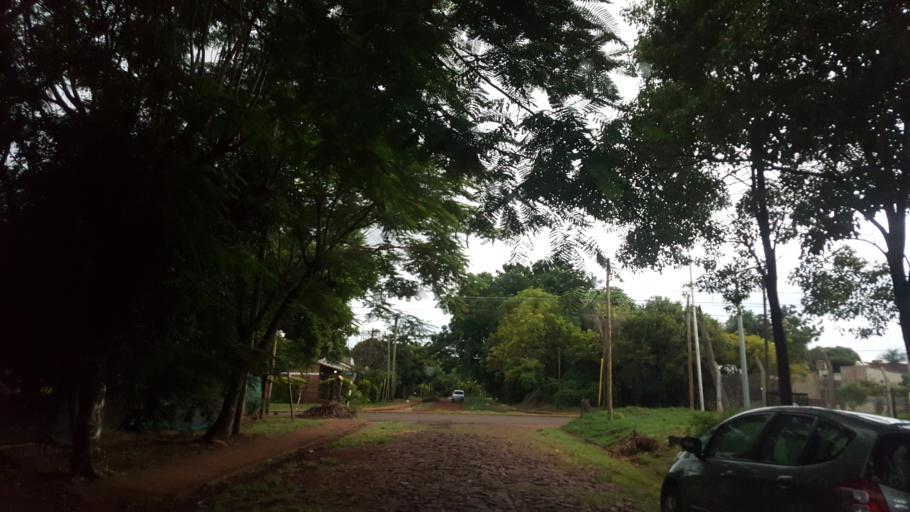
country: AR
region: Misiones
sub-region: Departamento de Capital
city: Posadas
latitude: -27.3971
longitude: -55.9425
